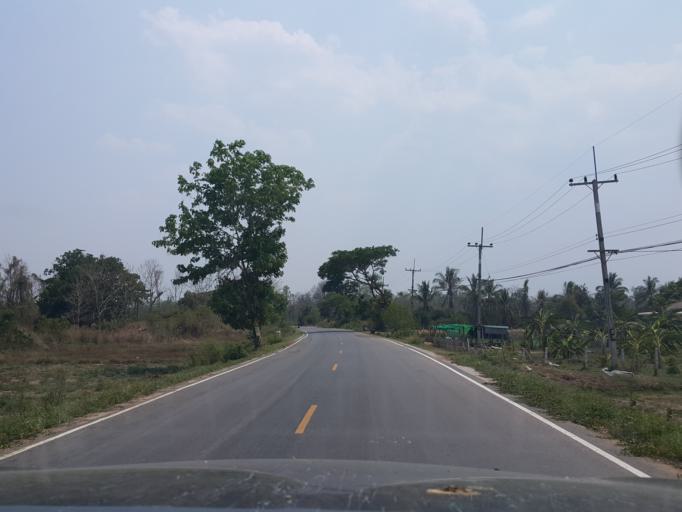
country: TH
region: Lampang
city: Mae Phrik
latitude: 17.4962
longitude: 99.1265
